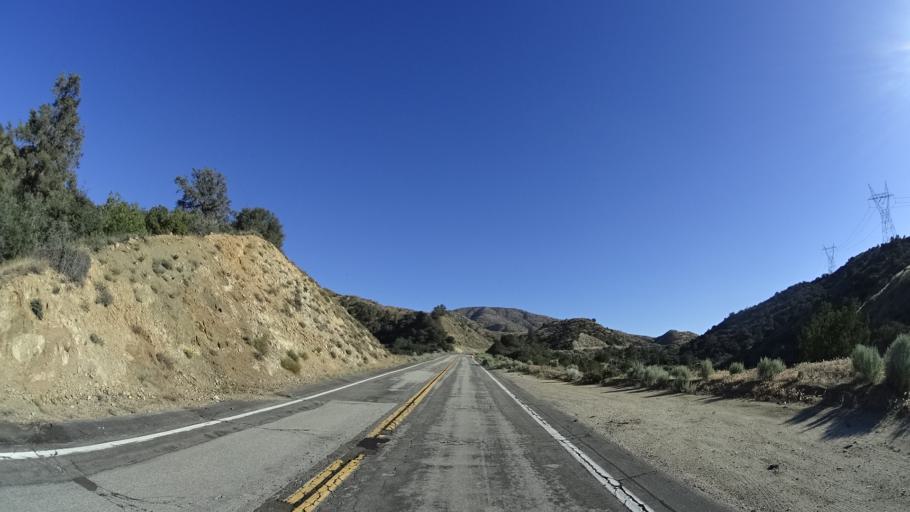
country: US
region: California
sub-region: Los Angeles County
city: Vincent
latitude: 34.4857
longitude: -118.0647
